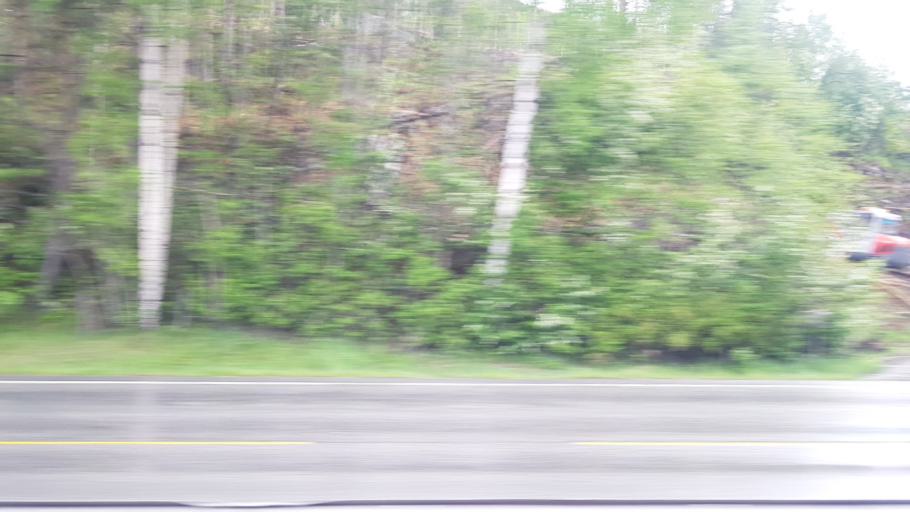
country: NO
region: Oppland
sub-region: Nord-Fron
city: Vinstra
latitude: 61.6067
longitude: 9.7260
